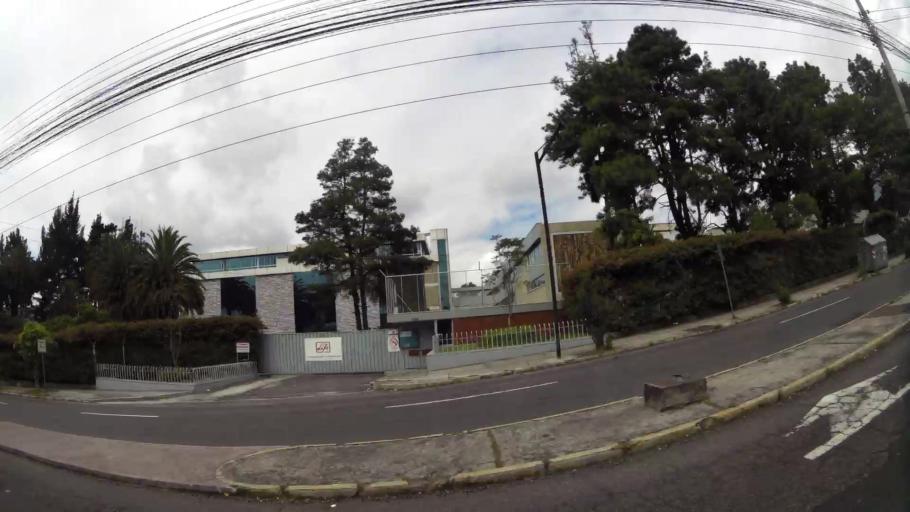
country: EC
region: Pichincha
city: Quito
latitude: -0.1598
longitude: -78.4886
